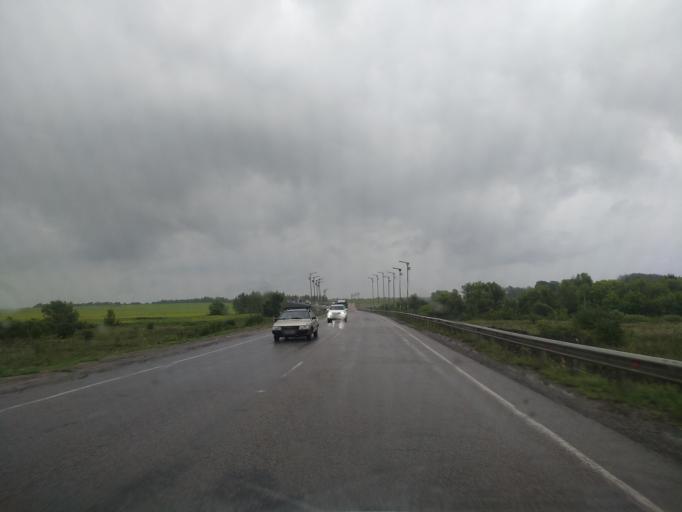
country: RU
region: Voronezj
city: Verkhnyaya Khava
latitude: 51.6751
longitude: 39.8166
